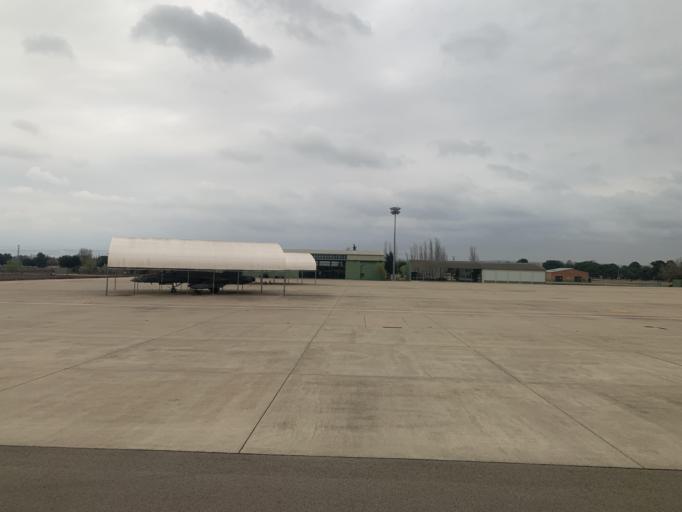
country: ES
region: Aragon
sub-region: Provincia de Zaragoza
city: Utebo
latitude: 41.6705
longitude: -1.0365
